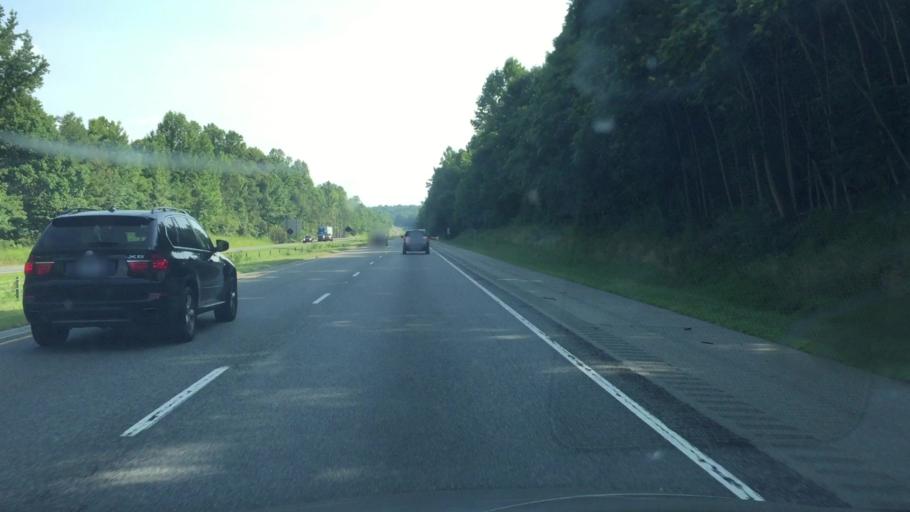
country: US
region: North Carolina
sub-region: Rockingham County
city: Reidsville
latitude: 36.3527
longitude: -79.6321
